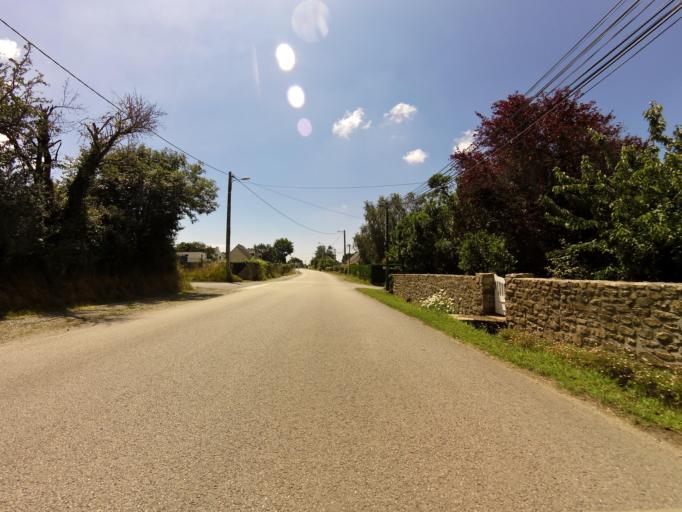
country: FR
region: Brittany
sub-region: Departement du Morbihan
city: Theix
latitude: 47.6089
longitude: -2.6802
